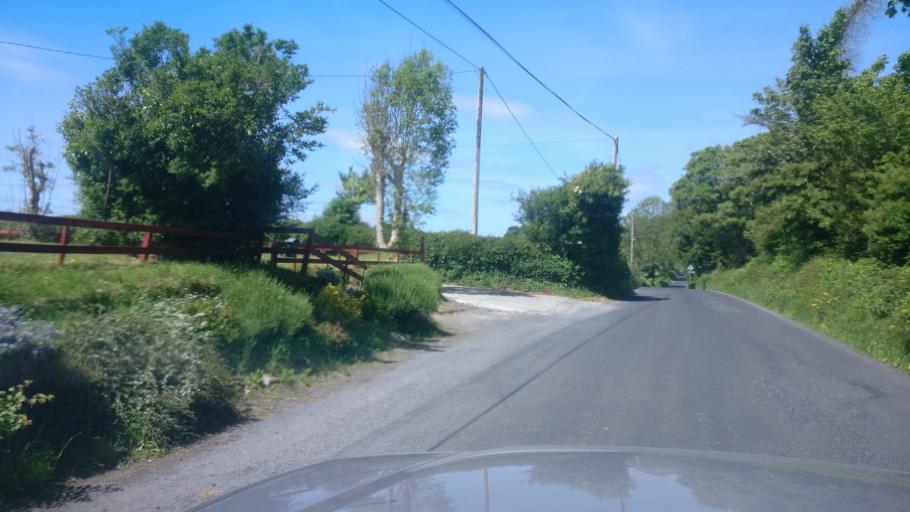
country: IE
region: Connaught
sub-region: County Galway
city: Gort
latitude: 53.0942
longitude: -8.8104
